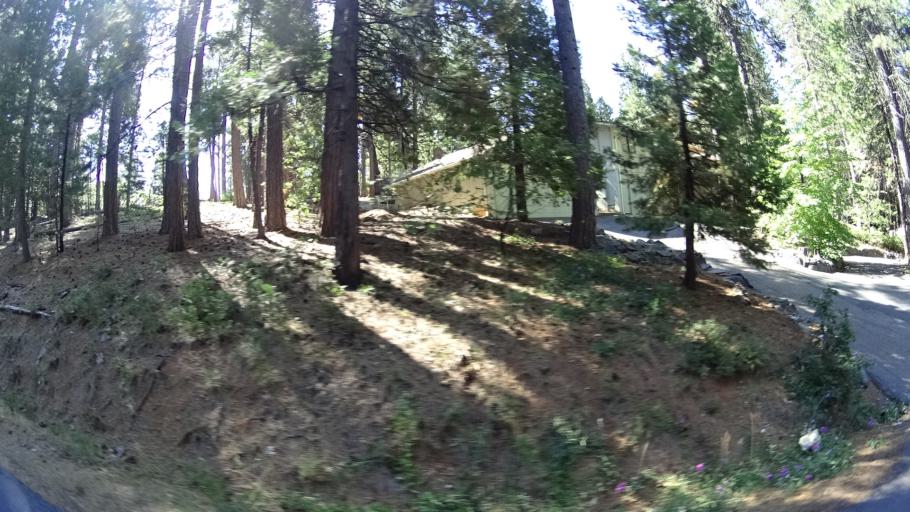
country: US
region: California
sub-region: Calaveras County
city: Arnold
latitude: 38.2439
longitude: -120.3698
